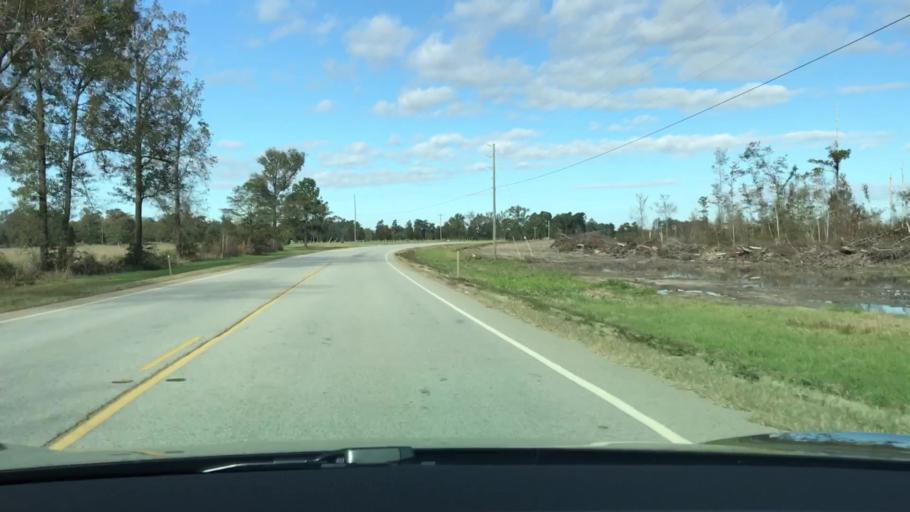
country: US
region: Georgia
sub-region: Jefferson County
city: Wrens
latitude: 33.1177
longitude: -82.4407
